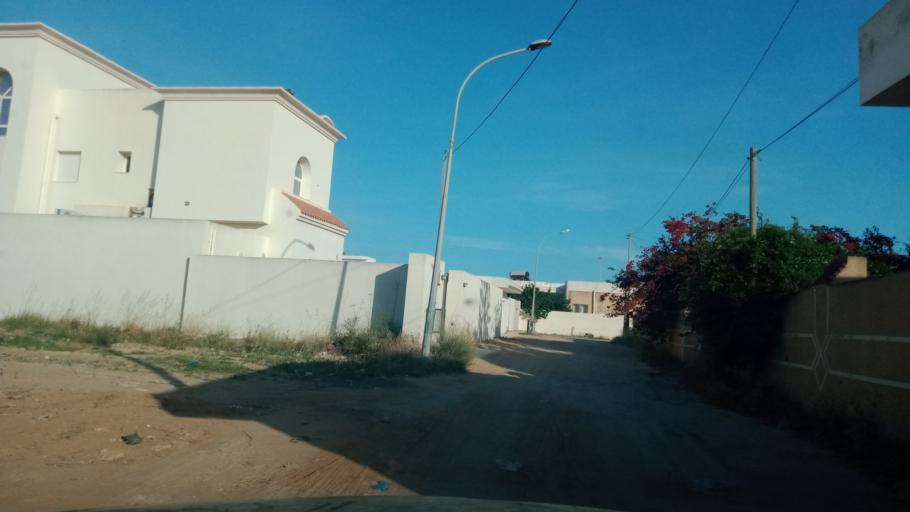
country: TN
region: Safaqis
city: Al Qarmadah
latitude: 34.8146
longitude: 10.7441
